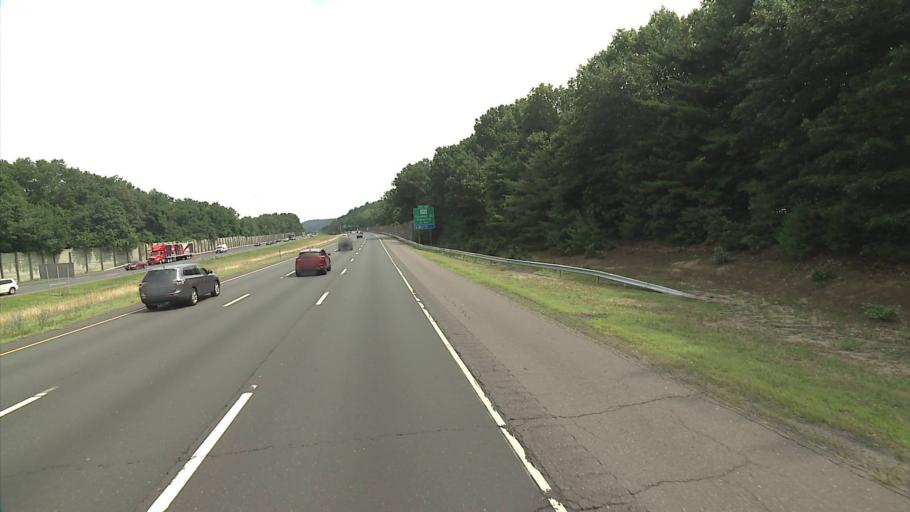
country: US
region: Connecticut
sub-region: Hartford County
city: Plainville
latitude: 41.6566
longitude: -72.8517
